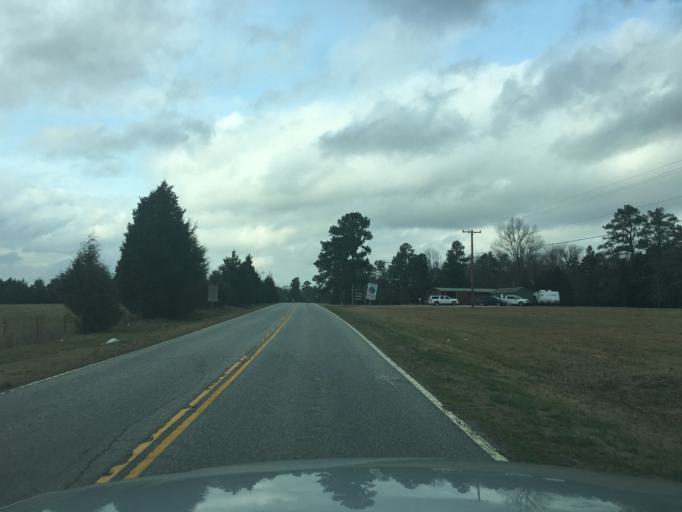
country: US
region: South Carolina
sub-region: Abbeville County
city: Abbeville
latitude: 34.2222
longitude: -82.3894
